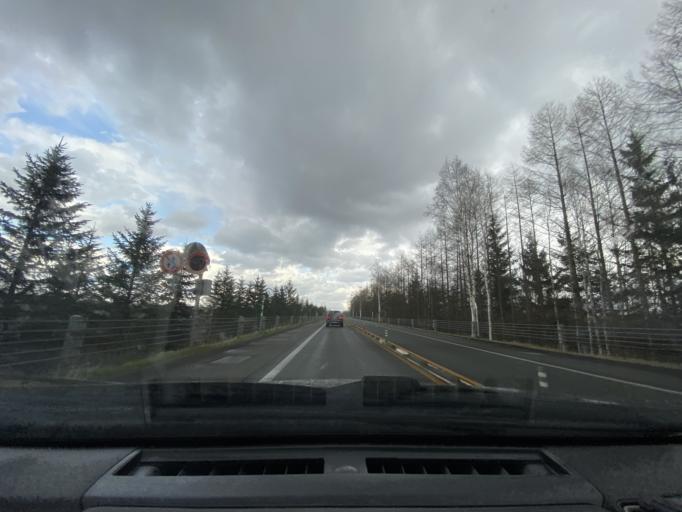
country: JP
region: Hokkaido
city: Otofuke
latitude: 42.9786
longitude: 142.9437
